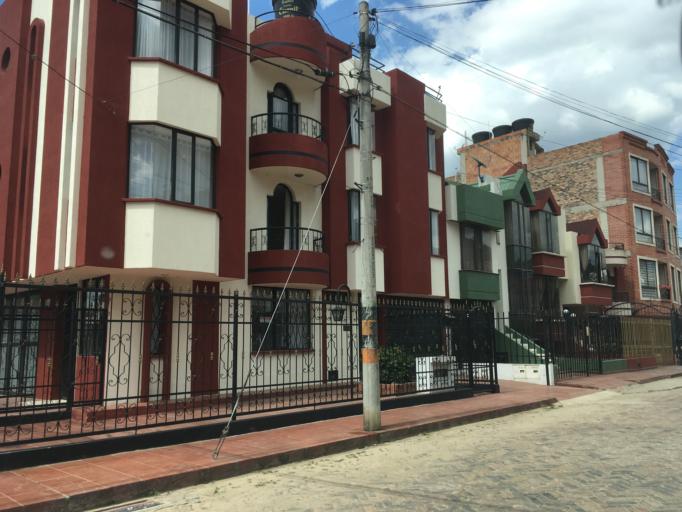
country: CO
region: Boyaca
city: Sogamoso
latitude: 5.7233
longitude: -72.9210
